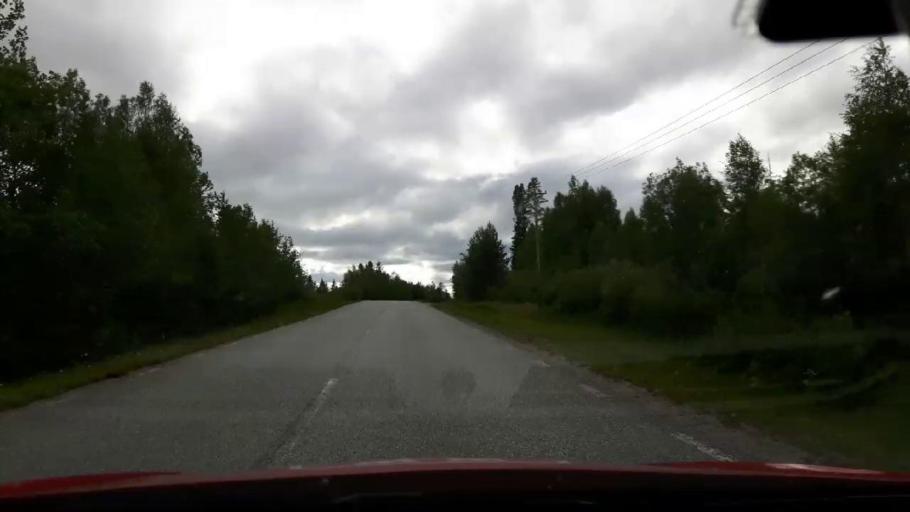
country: SE
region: Jaemtland
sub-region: Ragunda Kommun
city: Hammarstrand
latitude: 62.9649
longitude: 16.0054
